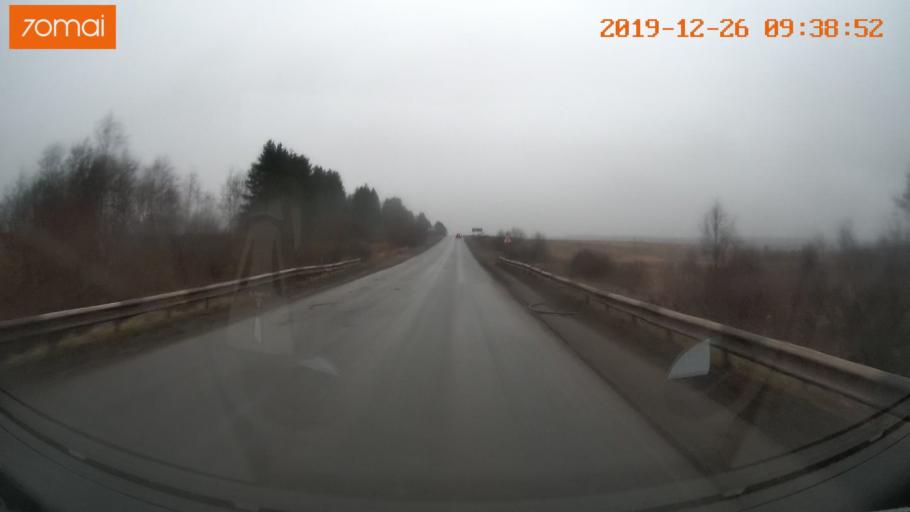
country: RU
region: Vologda
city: Vologda
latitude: 59.1487
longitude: 40.0349
